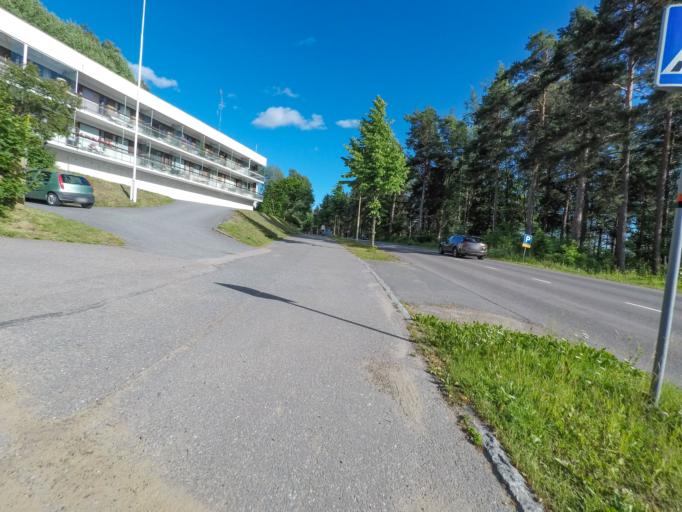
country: FI
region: South Karelia
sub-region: Lappeenranta
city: Lappeenranta
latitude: 61.0663
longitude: 28.1584
